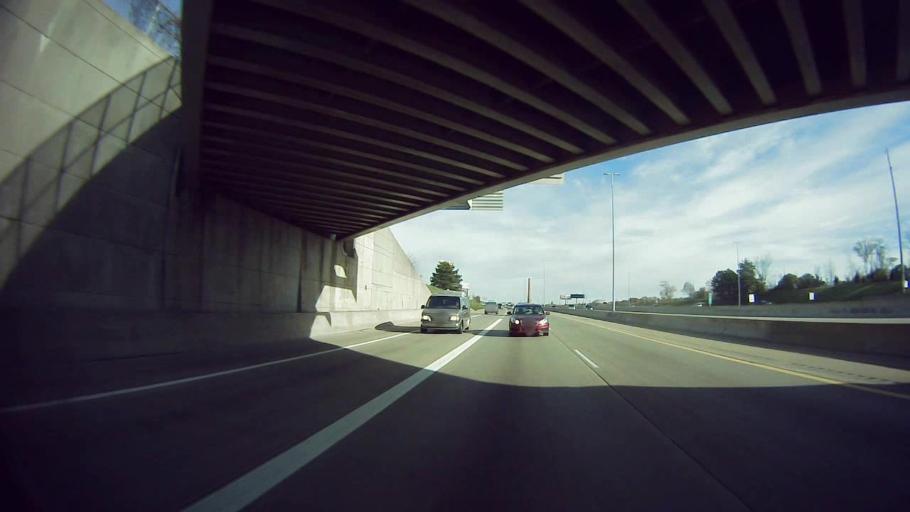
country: US
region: Michigan
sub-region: Wayne County
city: Dearborn Heights
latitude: 42.3783
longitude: -83.2307
